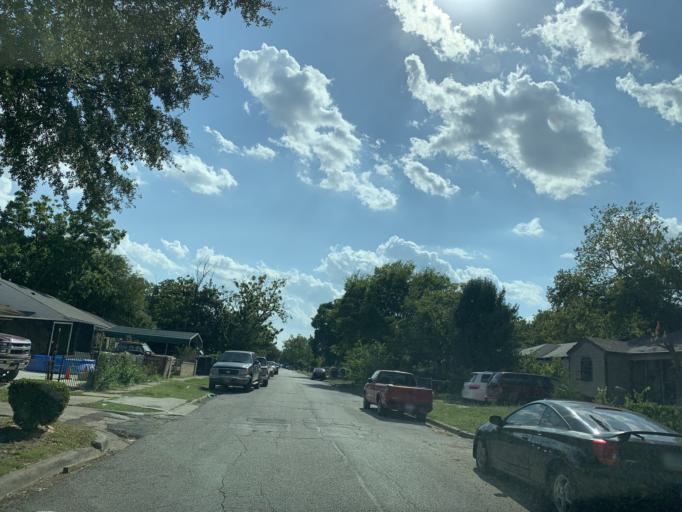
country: US
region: Texas
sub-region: Dallas County
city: Dallas
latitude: 32.7068
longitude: -96.7776
